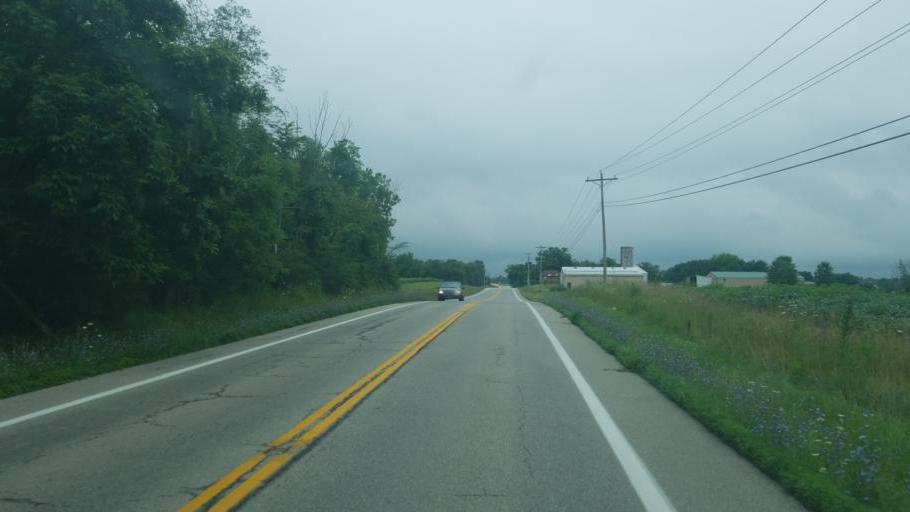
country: US
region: Ohio
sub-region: Delaware County
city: Sunbury
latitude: 40.3163
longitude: -82.8448
